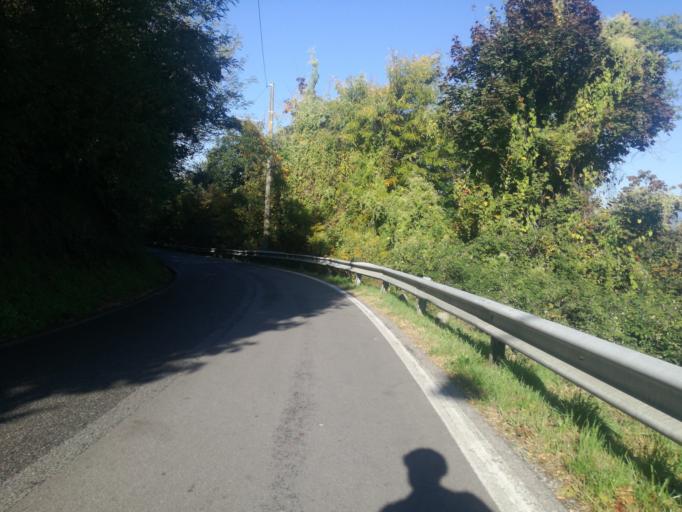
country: IT
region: Lombardy
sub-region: Citta metropolitana di Milano
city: Trezzo sull'Adda
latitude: 45.6147
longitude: 9.5150
